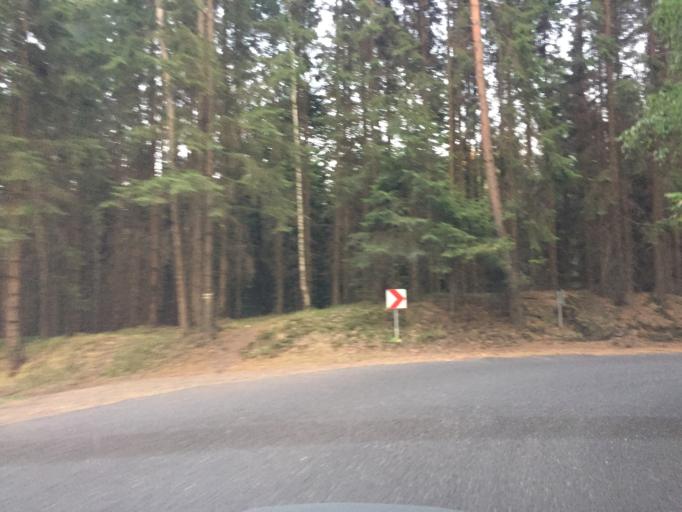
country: CZ
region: Ustecky
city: Ceska Kamenice
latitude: 50.8563
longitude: 14.3767
